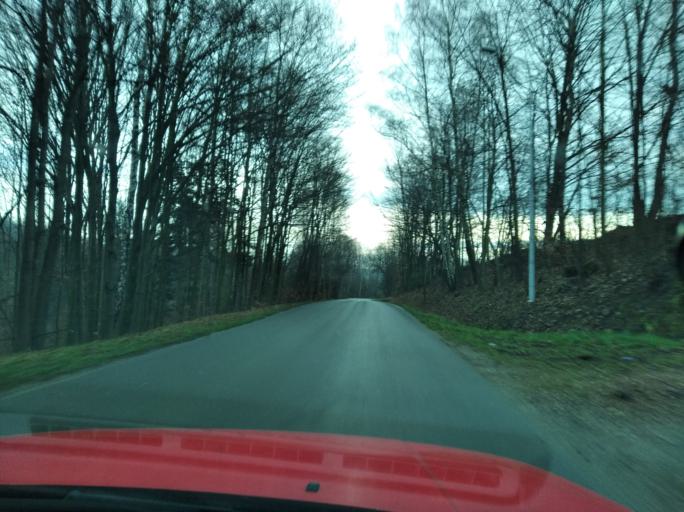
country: PL
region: Subcarpathian Voivodeship
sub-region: Powiat strzyzowski
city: Jawornik
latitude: 49.8725
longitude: 21.8706
